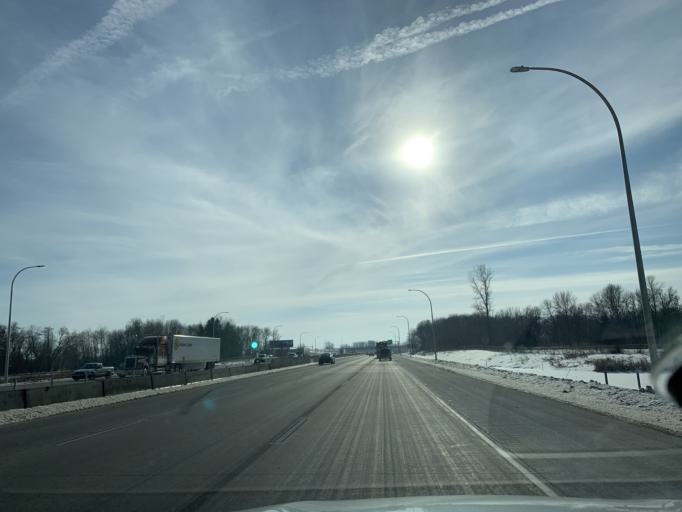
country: US
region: Minnesota
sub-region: Washington County
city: Forest Lake
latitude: 45.2861
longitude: -93.0033
